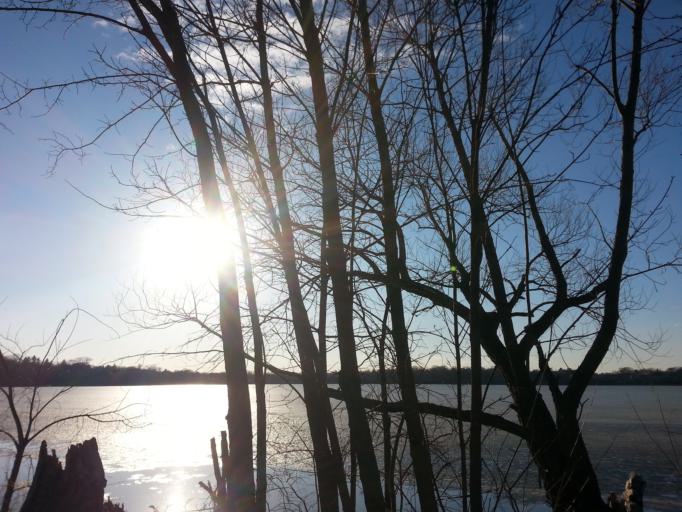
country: US
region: Minnesota
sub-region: Hennepin County
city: Richfield
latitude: 44.9176
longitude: -93.2999
